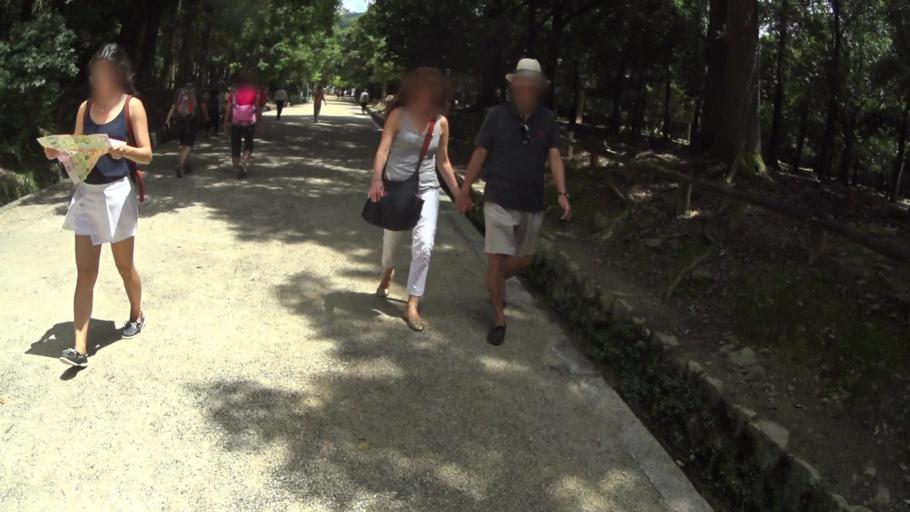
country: JP
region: Nara
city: Nara-shi
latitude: 34.6821
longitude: 135.8418
